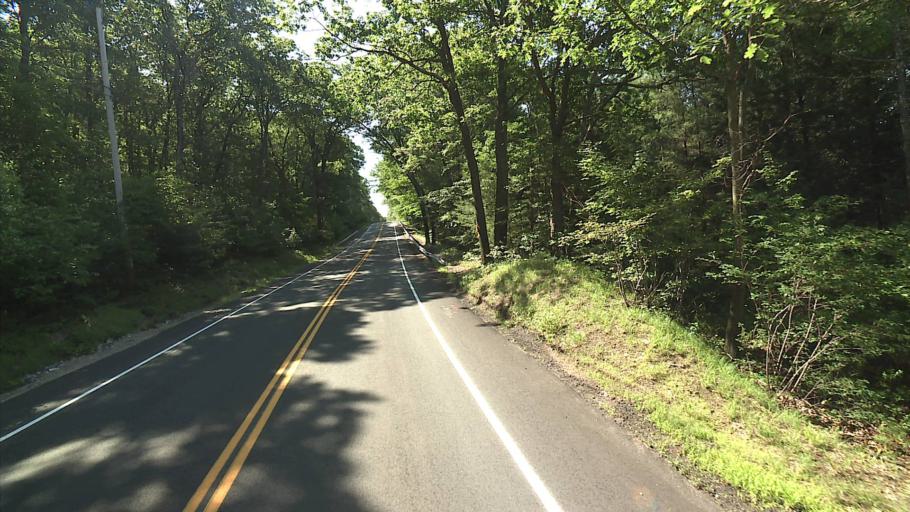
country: US
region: Connecticut
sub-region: Litchfield County
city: Northwest Harwinton
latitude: 41.7480
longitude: -73.0205
